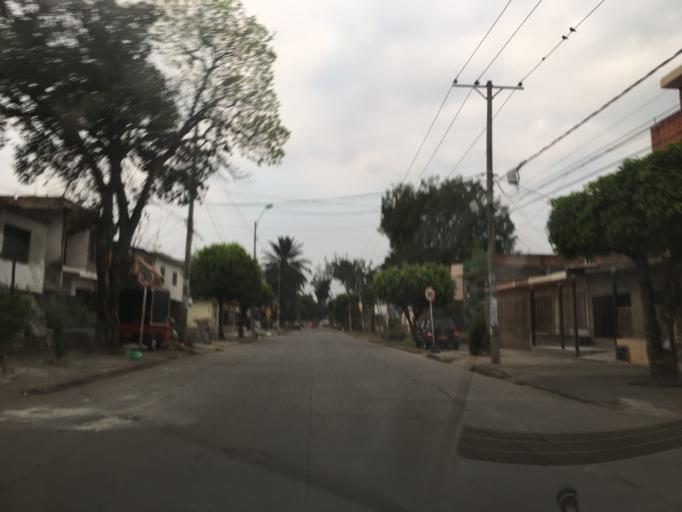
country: CO
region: Valle del Cauca
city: Cali
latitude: 3.4150
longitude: -76.5225
